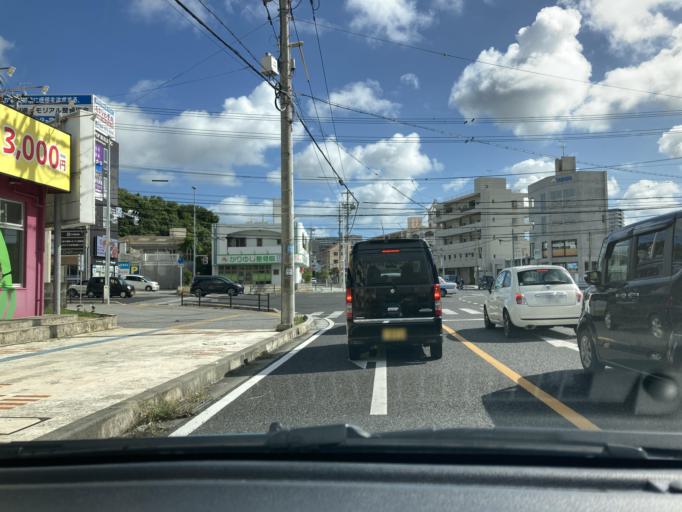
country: JP
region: Okinawa
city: Tomigusuku
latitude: 26.1960
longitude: 127.7271
